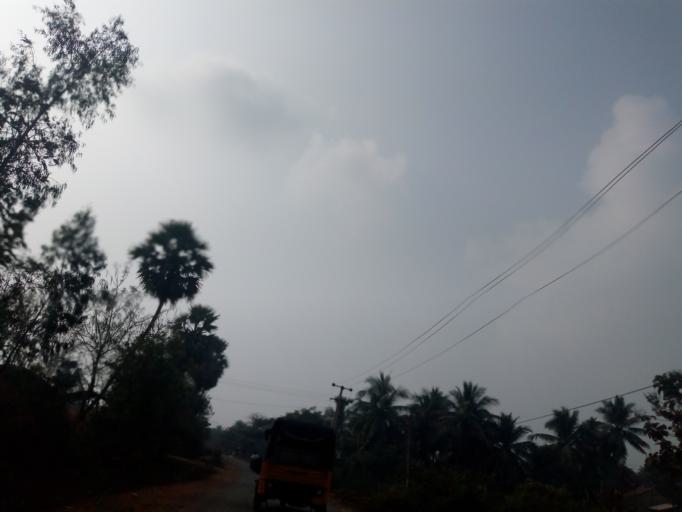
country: IN
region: Andhra Pradesh
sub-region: West Godavari
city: Tadepallegudem
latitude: 16.8188
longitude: 81.3626
